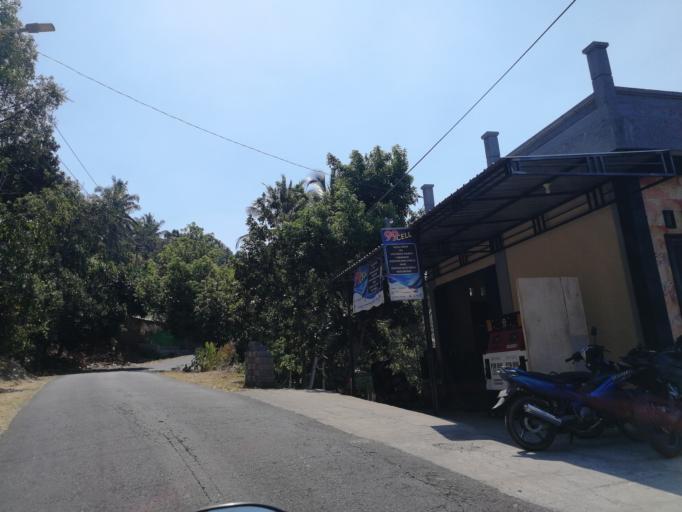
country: ID
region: Bali
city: Banjar Kedisan
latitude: -8.1431
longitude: 115.3135
